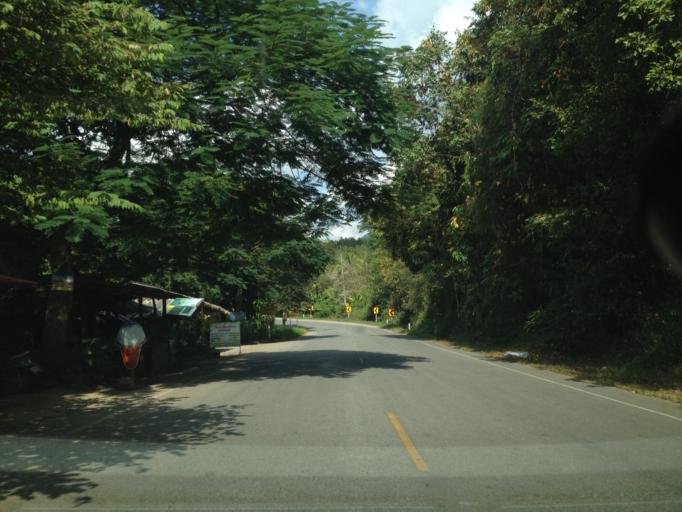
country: TH
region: Chiang Mai
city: Hang Dong
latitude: 18.7675
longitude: 98.8699
